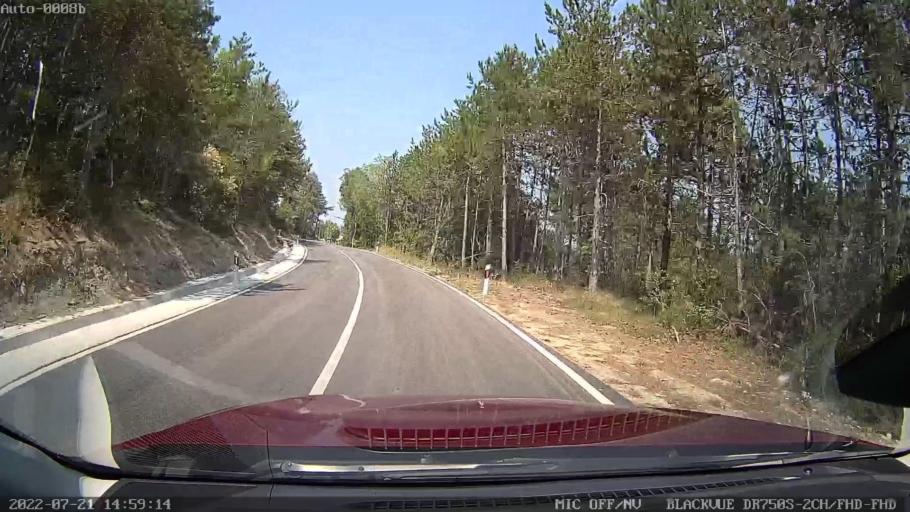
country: HR
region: Istarska
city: Pazin
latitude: 45.2177
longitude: 13.9584
